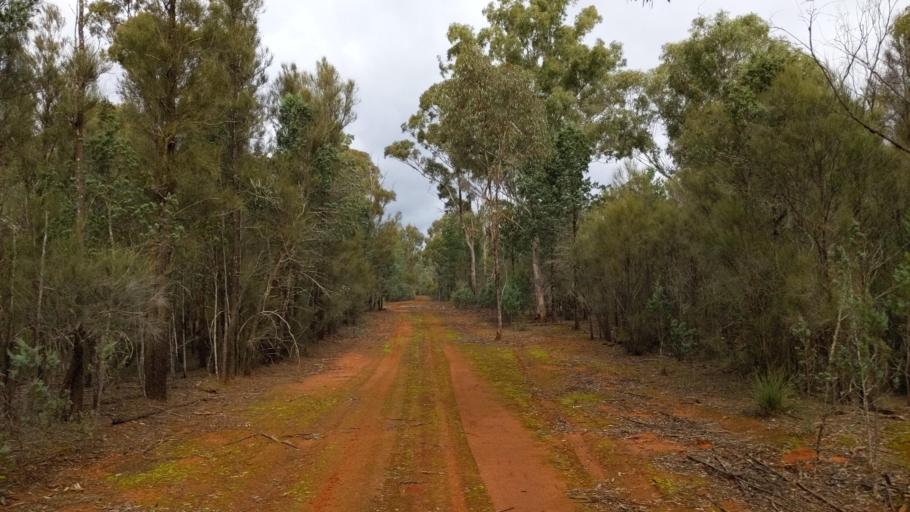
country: AU
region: New South Wales
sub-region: Coolamon
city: Coolamon
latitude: -34.8341
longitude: 146.9349
